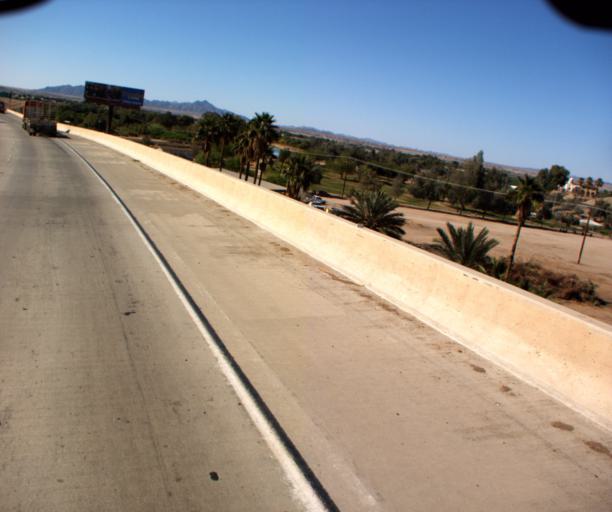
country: US
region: Arizona
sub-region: Yuma County
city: Yuma
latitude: 32.7287
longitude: -114.6178
